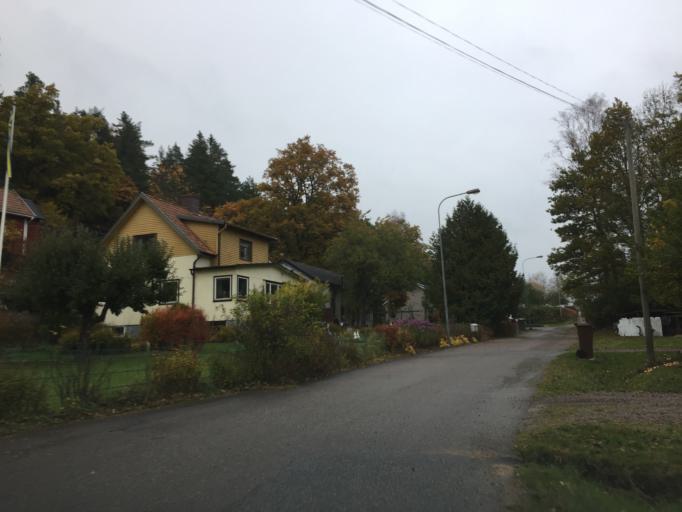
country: SE
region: Vaestra Goetaland
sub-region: Trollhattan
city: Sjuntorp
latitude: 58.1973
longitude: 12.2433
